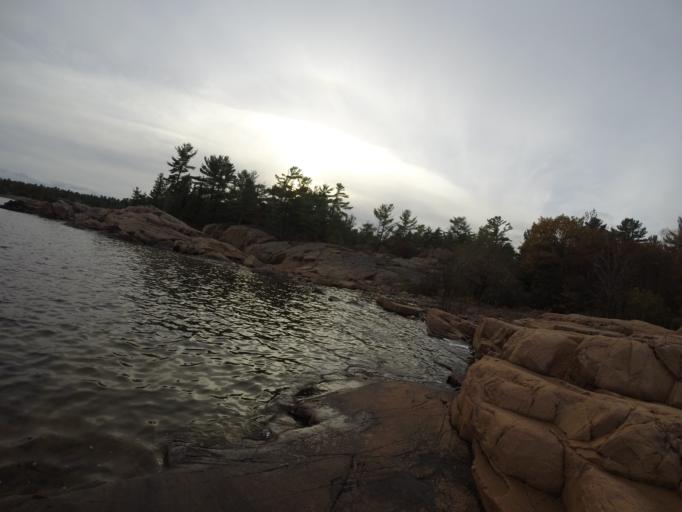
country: CA
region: Ontario
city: Espanola
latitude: 45.9693
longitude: -81.4983
